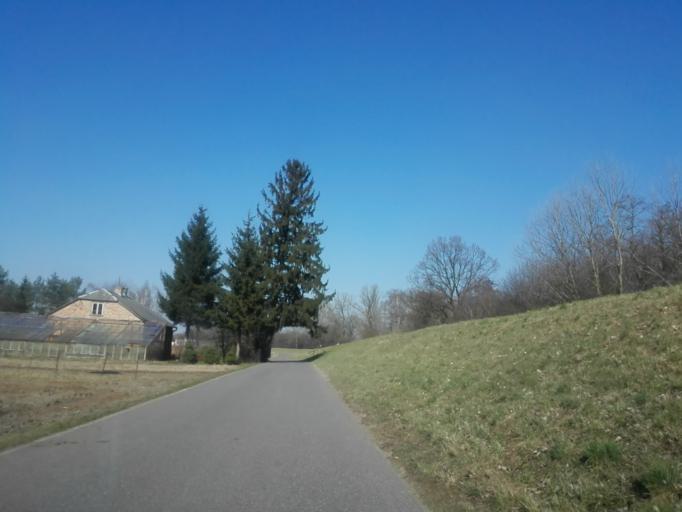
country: PL
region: Masovian Voivodeship
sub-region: Powiat piaseczynski
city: Konstancin-Jeziorna
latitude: 52.1242
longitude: 21.1732
